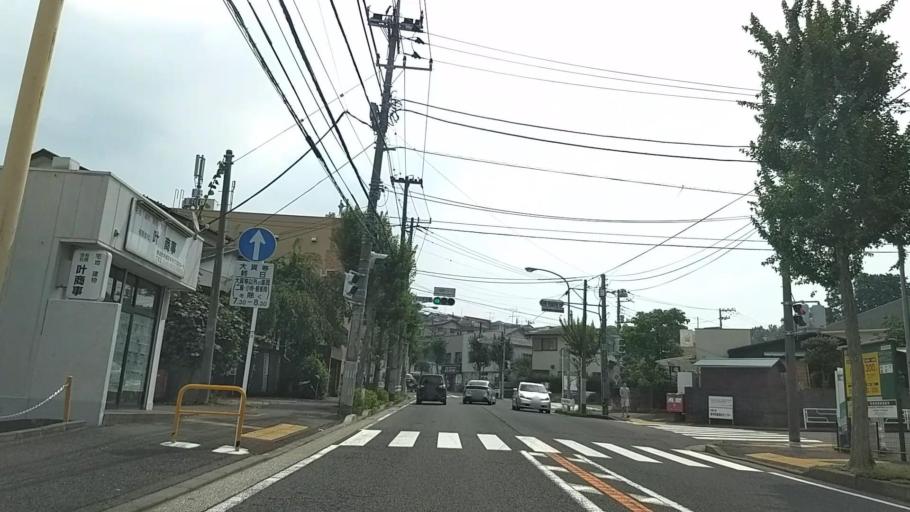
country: JP
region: Kanagawa
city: Yokohama
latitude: 35.4241
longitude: 139.5740
